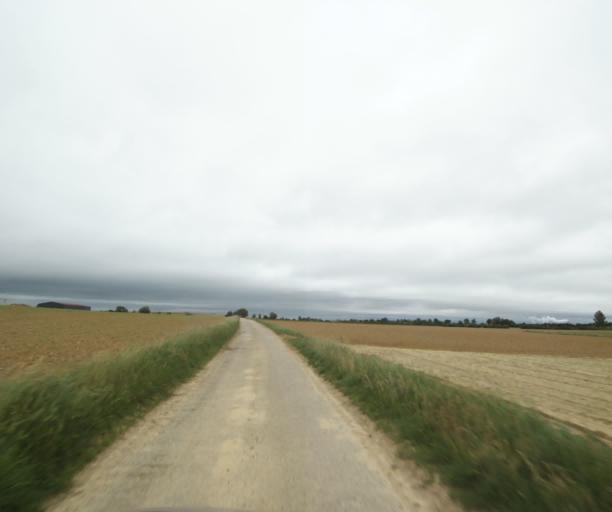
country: FR
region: Rhone-Alpes
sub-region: Departement de l'Ain
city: Miribel
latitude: 45.8365
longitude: 4.9344
